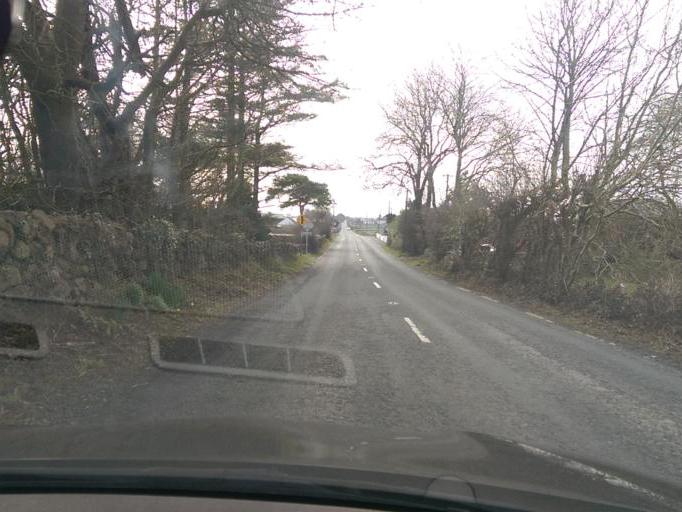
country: IE
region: Connaught
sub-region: County Galway
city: Tuam
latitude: 53.4003
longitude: -8.8313
